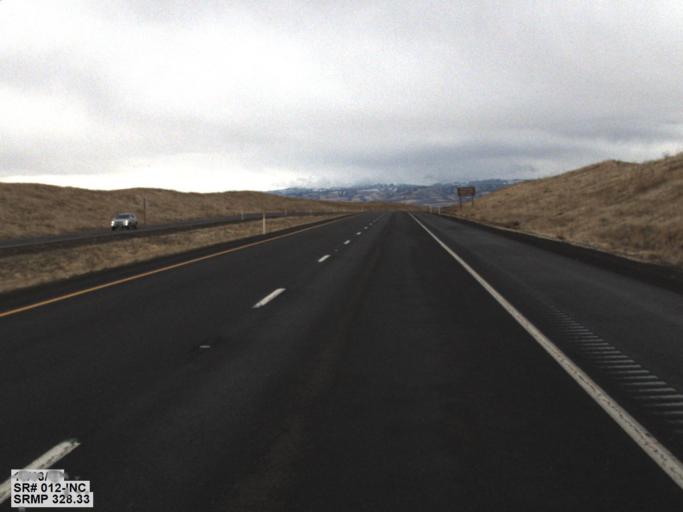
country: US
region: Washington
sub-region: Walla Walla County
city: Garrett
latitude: 46.0512
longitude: -118.5051
